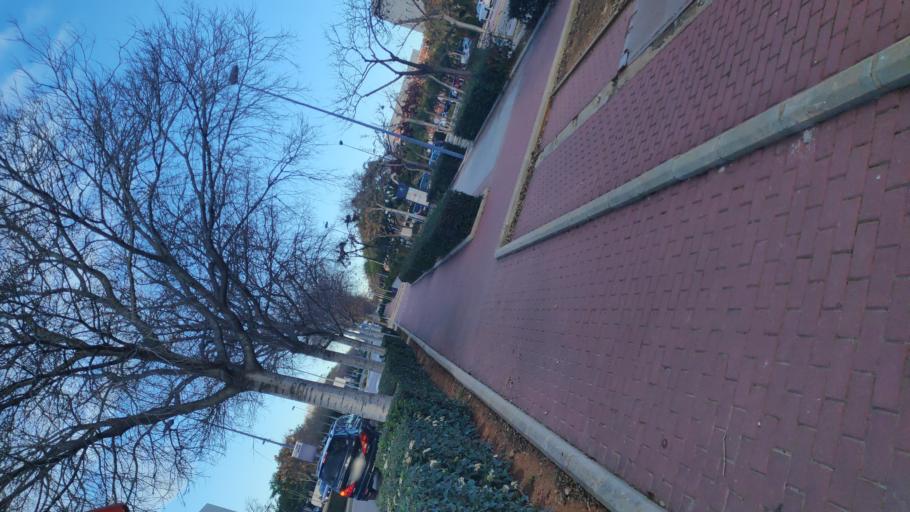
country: ES
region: Valencia
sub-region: Provincia de Castello
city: Castello de la Plana
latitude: 39.9925
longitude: -0.0691
